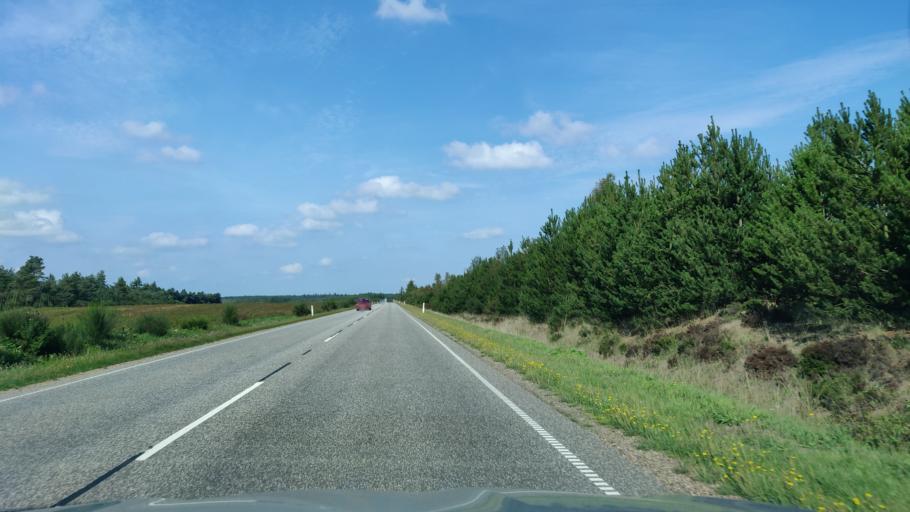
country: DK
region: Central Jutland
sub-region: Herning Kommune
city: Sunds
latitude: 56.3402
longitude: 8.9801
